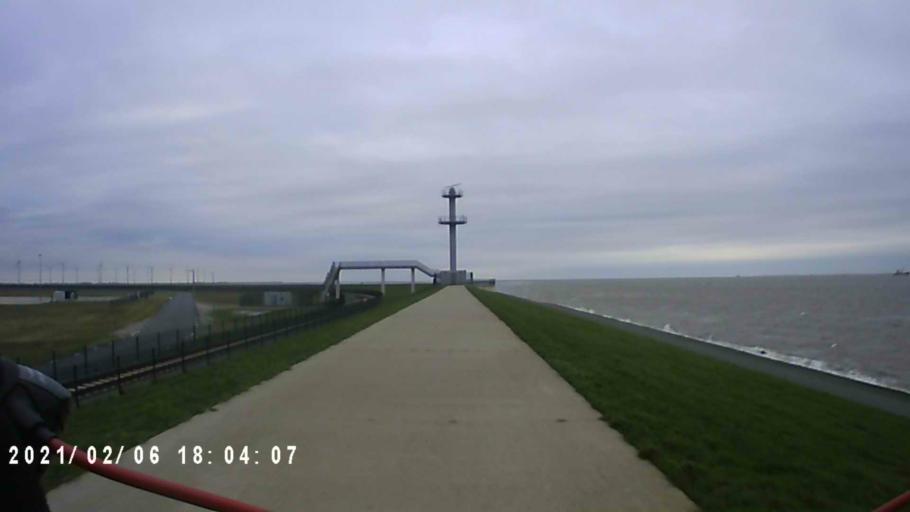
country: NL
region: Groningen
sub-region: Gemeente Appingedam
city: Appingedam
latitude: 53.4622
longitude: 6.8173
